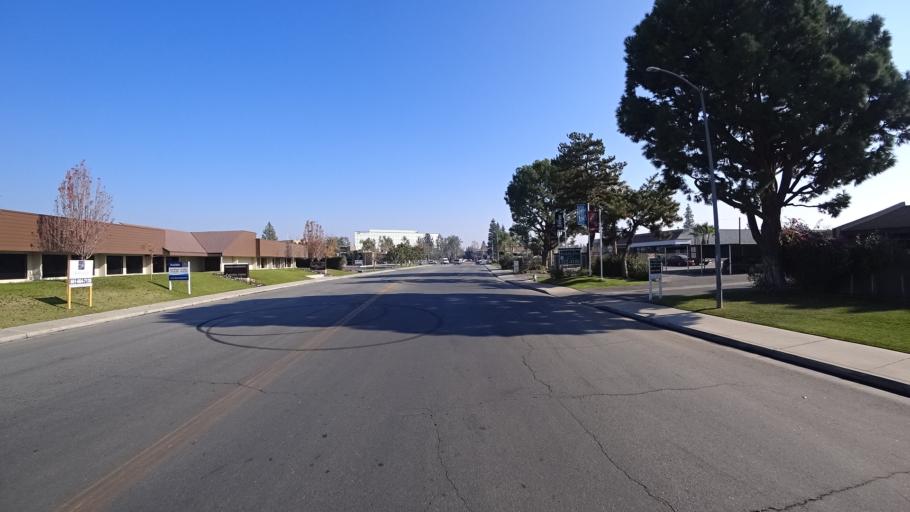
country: US
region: California
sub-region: Kern County
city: Bakersfield
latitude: 35.3589
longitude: -119.0630
